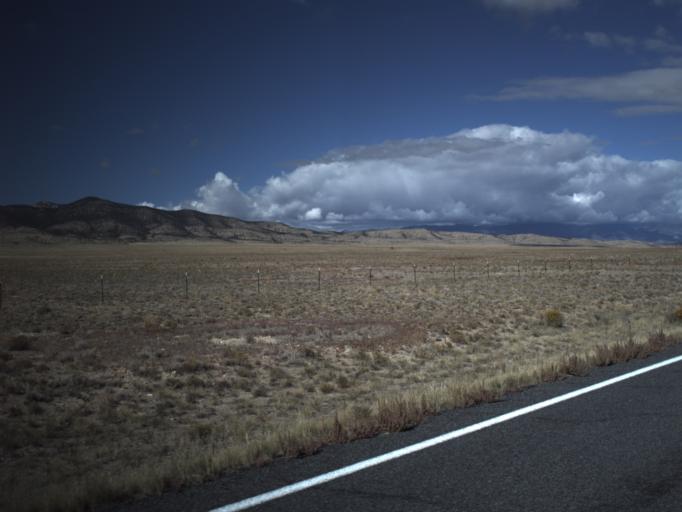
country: US
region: Utah
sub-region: Beaver County
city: Milford
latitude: 38.6435
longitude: -113.8637
